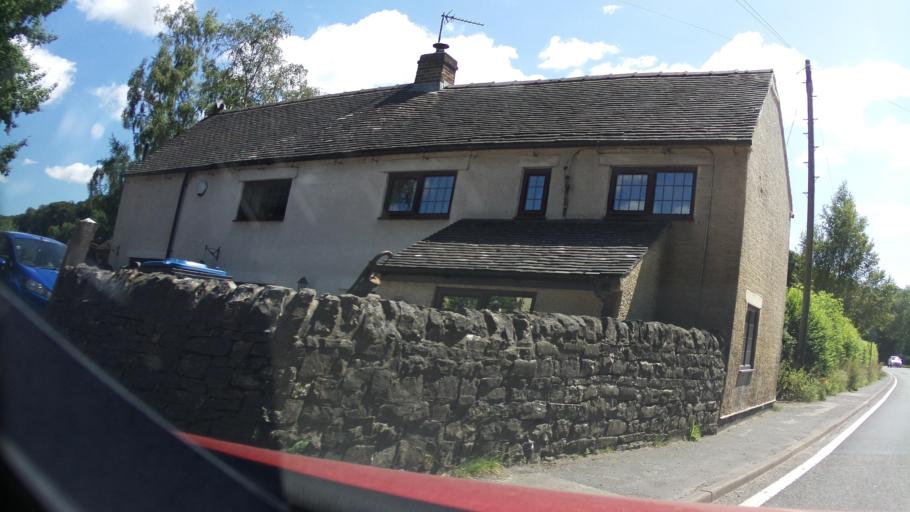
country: GB
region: England
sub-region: Derbyshire
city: Ashbourne
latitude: 53.0472
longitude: -1.7396
